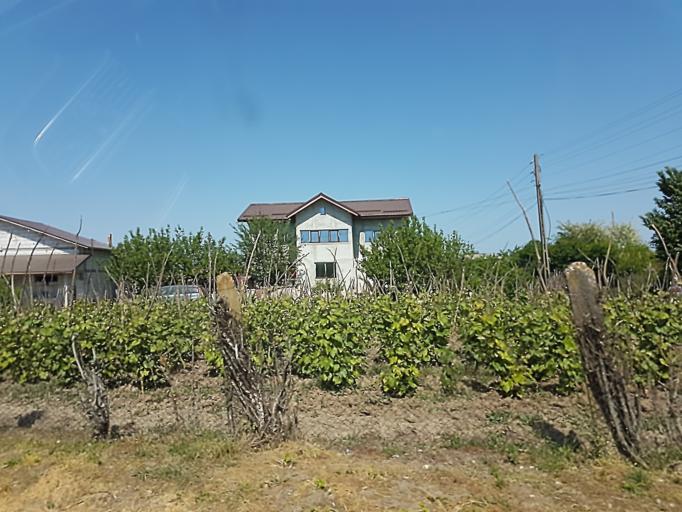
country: RO
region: Giurgiu
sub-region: Comuna Herasti
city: Herasti
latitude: 44.2153
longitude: 26.3588
